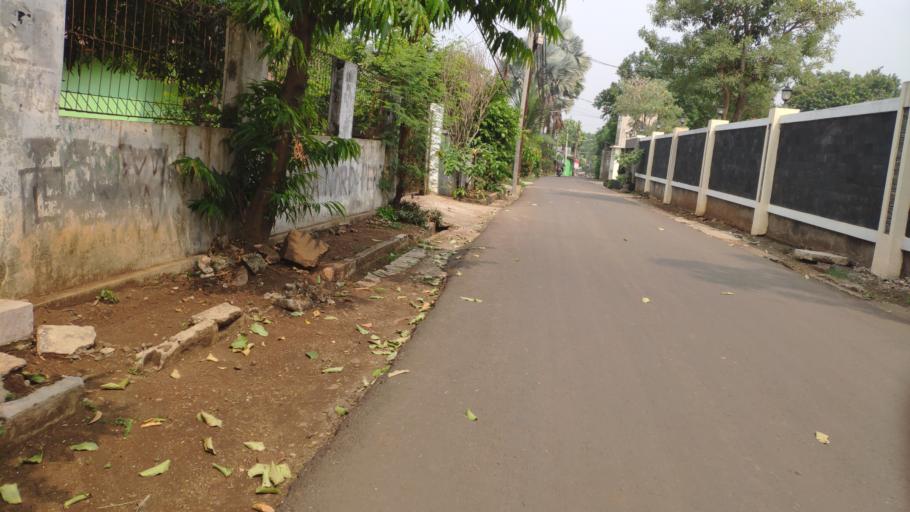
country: ID
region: West Java
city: Depok
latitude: -6.3369
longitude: 106.8196
